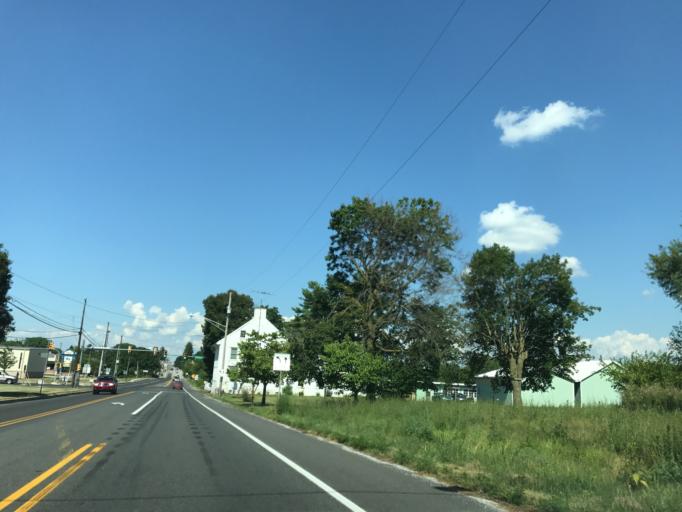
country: US
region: Pennsylvania
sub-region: Adams County
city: McSherrystown
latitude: 39.7981
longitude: -77.0319
